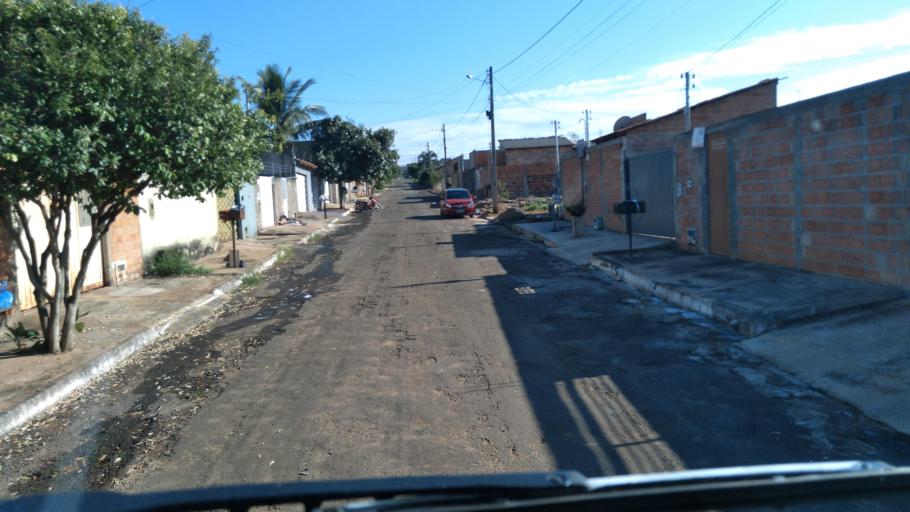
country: BR
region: Goias
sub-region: Mineiros
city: Mineiros
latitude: -17.5785
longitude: -52.5688
